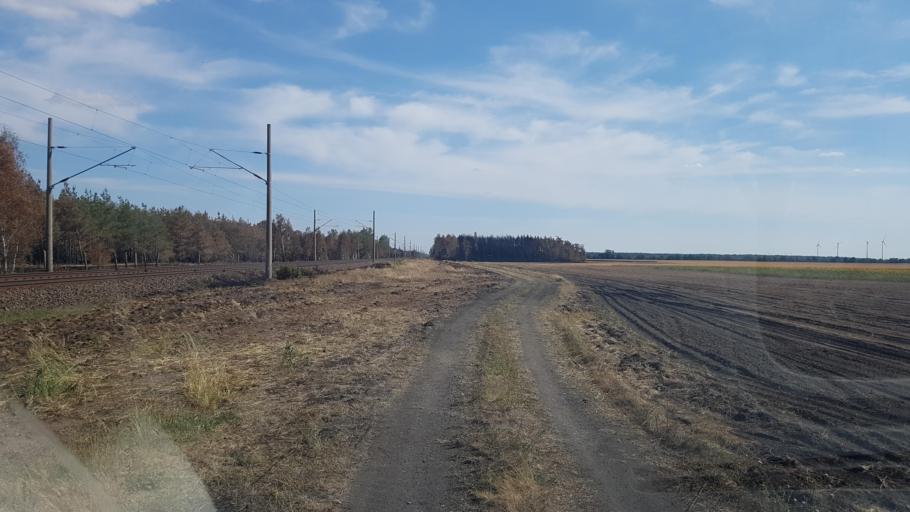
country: DE
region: Brandenburg
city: Muhlberg
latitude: 51.4332
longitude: 13.3043
